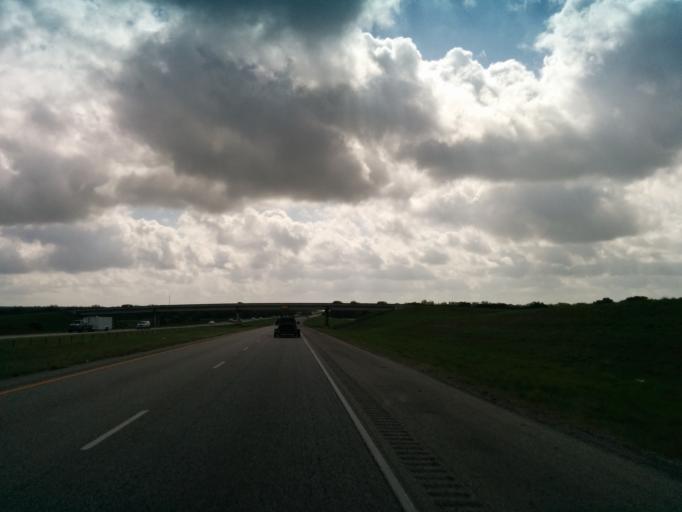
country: US
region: Texas
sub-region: Gonzales County
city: Waelder
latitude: 29.6615
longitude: -97.3908
